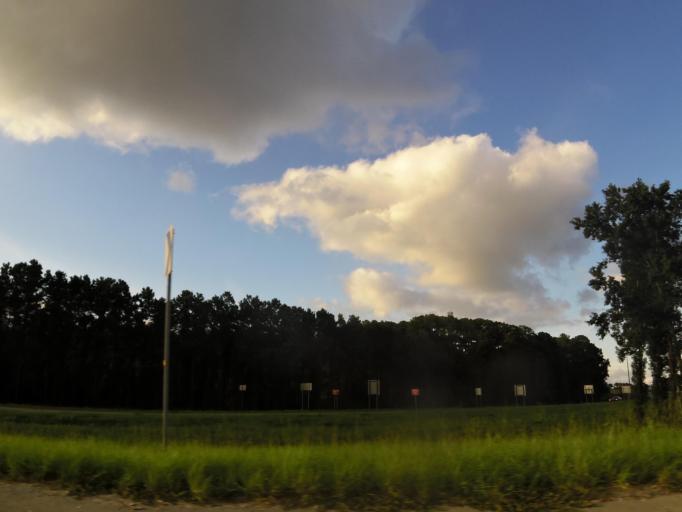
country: US
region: Georgia
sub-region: Glynn County
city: Brunswick
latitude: 31.1396
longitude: -81.5755
